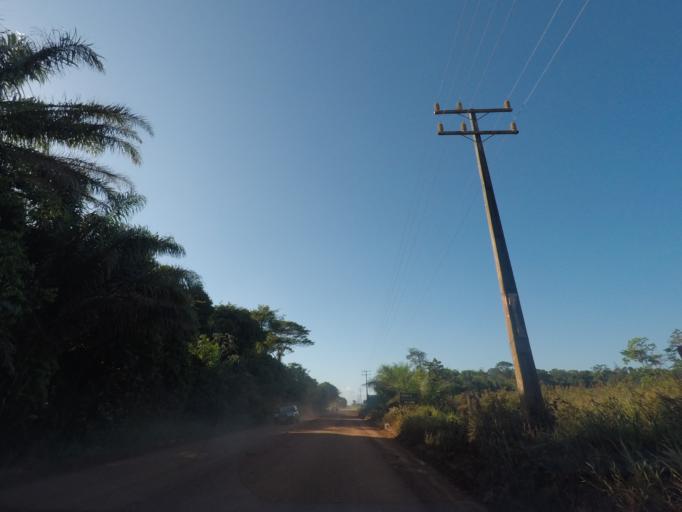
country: BR
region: Bahia
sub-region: Camamu
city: Camamu
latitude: -13.9446
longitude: -38.9477
